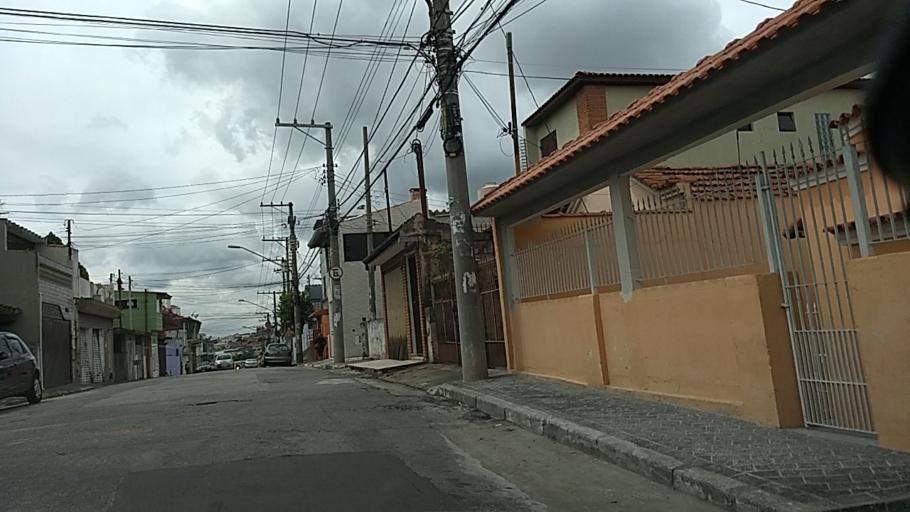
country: BR
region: Sao Paulo
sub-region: Guarulhos
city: Guarulhos
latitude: -23.4803
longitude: -46.5934
